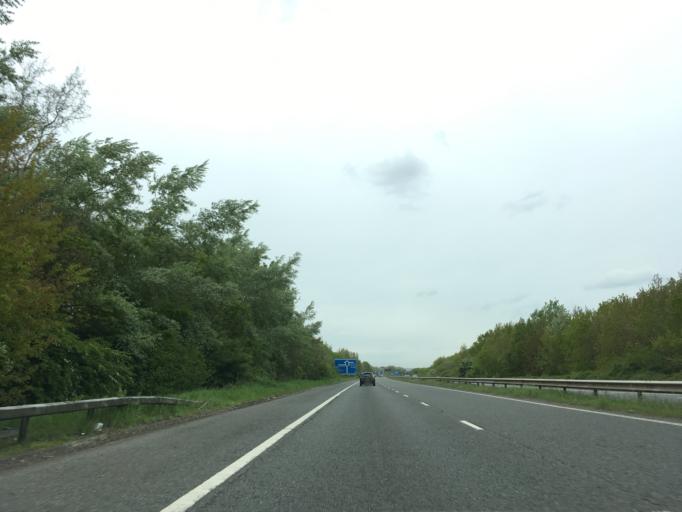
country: GB
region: England
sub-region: South Gloucestershire
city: Severn Beach
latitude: 51.5510
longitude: -2.6424
